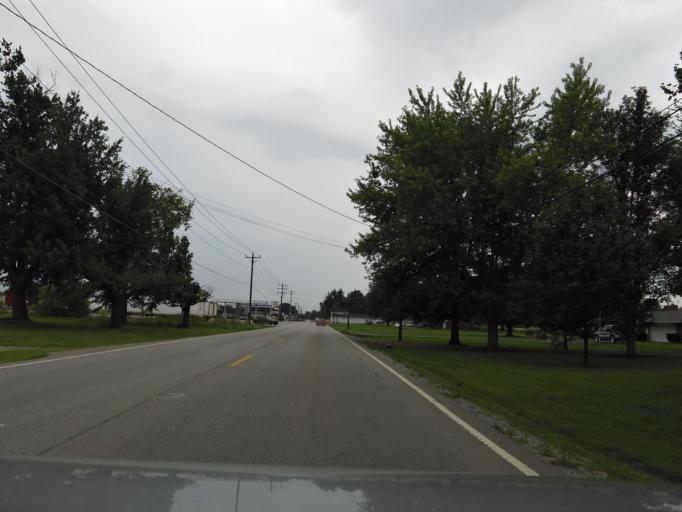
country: US
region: Ohio
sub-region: Brown County
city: Georgetown
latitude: 38.9155
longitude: -83.9031
